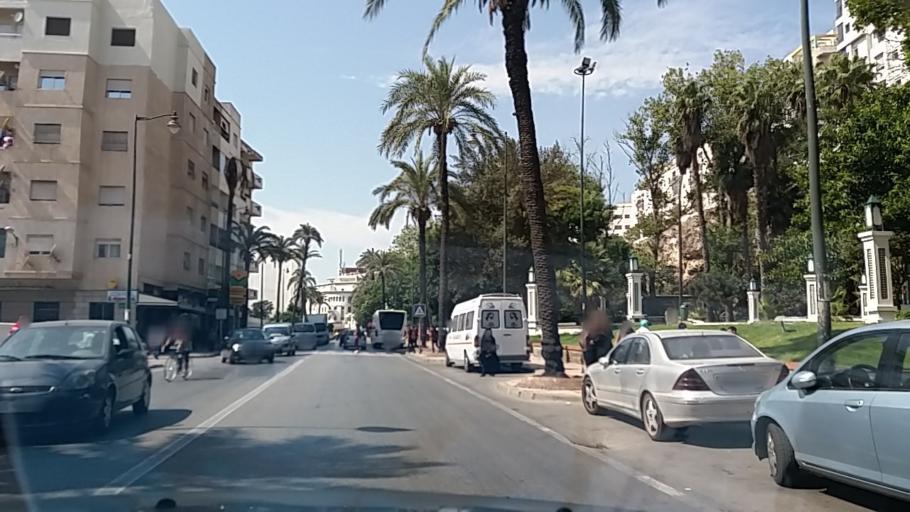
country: MA
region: Tanger-Tetouan
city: Tetouan
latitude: 35.5679
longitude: -5.3732
